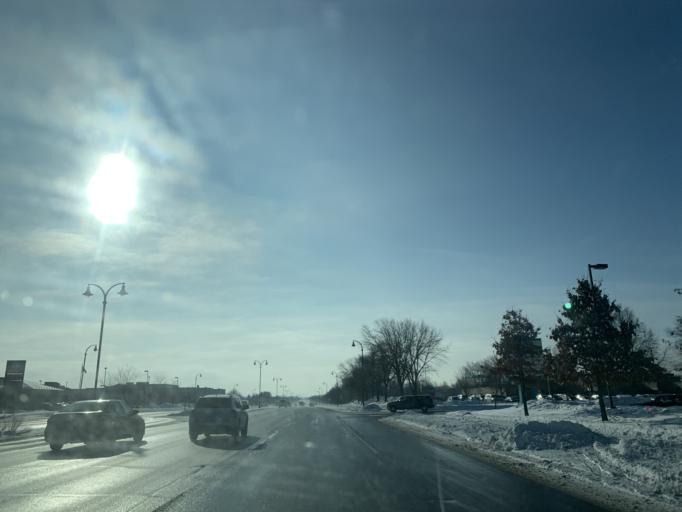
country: US
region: Minnesota
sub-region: Dakota County
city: Apple Valley
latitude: 44.7252
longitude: -93.2179
